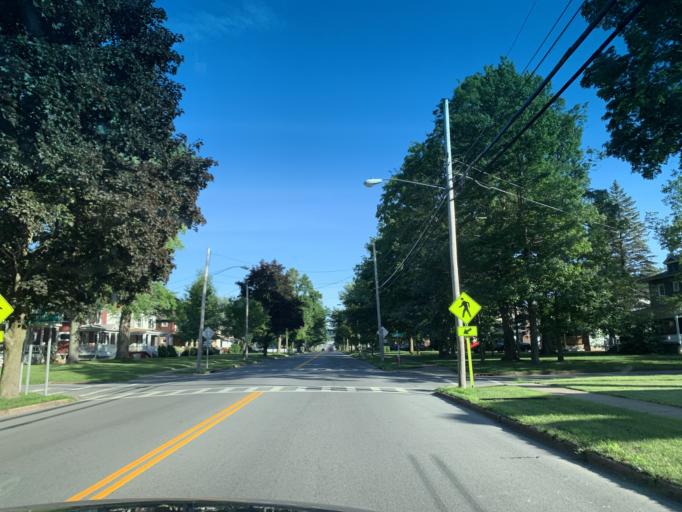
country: US
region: New York
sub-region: Madison County
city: Oneida
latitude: 43.0834
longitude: -75.6448
